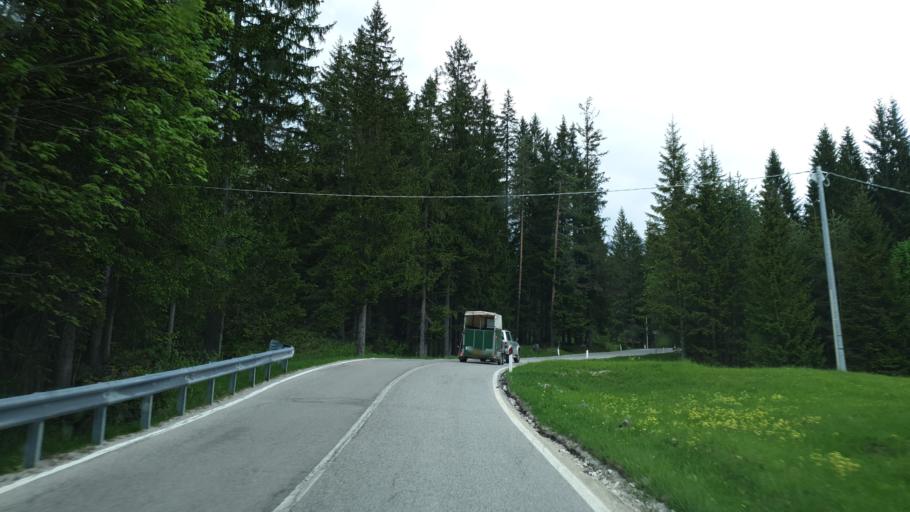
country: IT
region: Veneto
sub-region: Provincia di Belluno
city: San Vito
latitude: 46.5414
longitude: 12.2536
